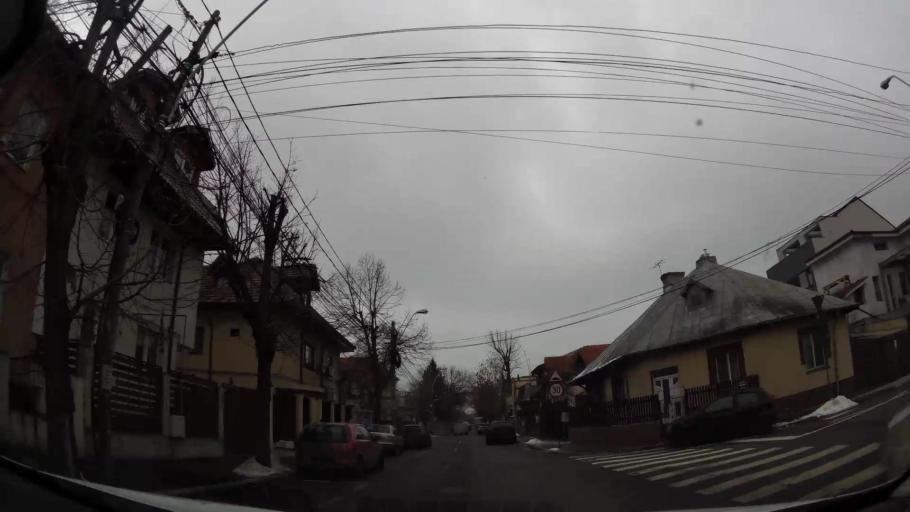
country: RO
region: Bucuresti
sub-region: Municipiul Bucuresti
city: Bucuresti
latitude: 44.4620
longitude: 26.0624
